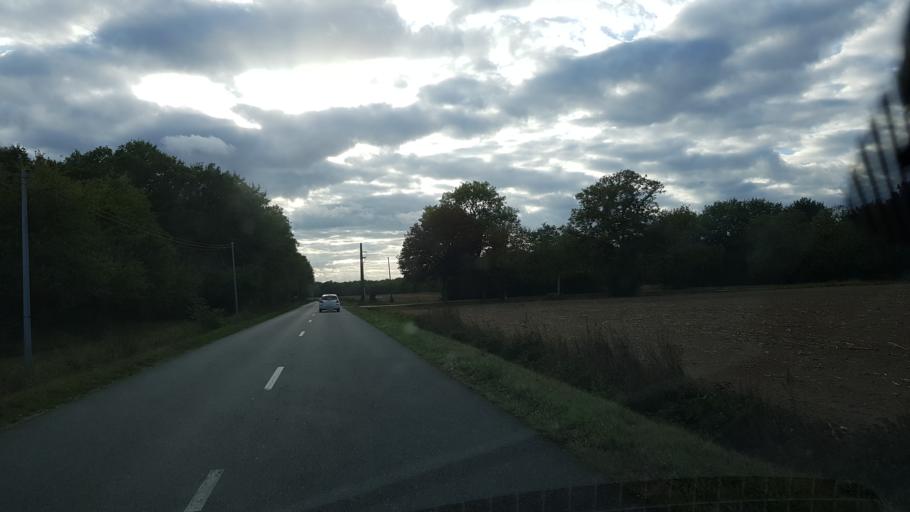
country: FR
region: Centre
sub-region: Departement du Loiret
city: Cerdon
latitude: 47.7015
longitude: 2.3014
